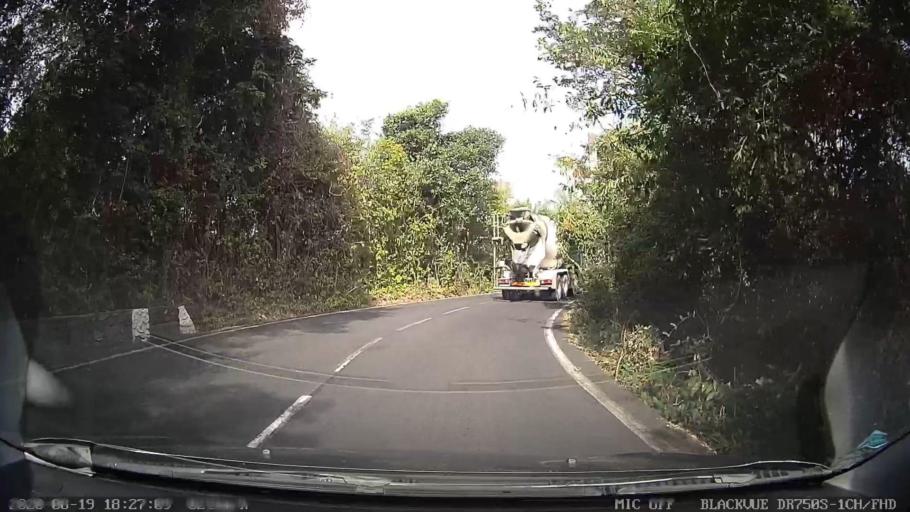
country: RE
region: Reunion
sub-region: Reunion
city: La Possession
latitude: -20.9550
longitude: 55.3510
